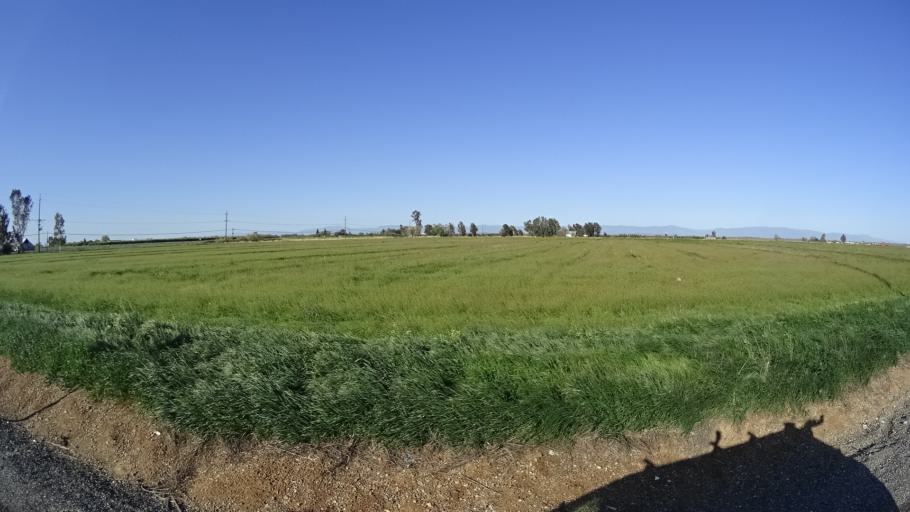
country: US
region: California
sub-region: Glenn County
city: Orland
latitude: 39.7700
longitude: -122.1107
